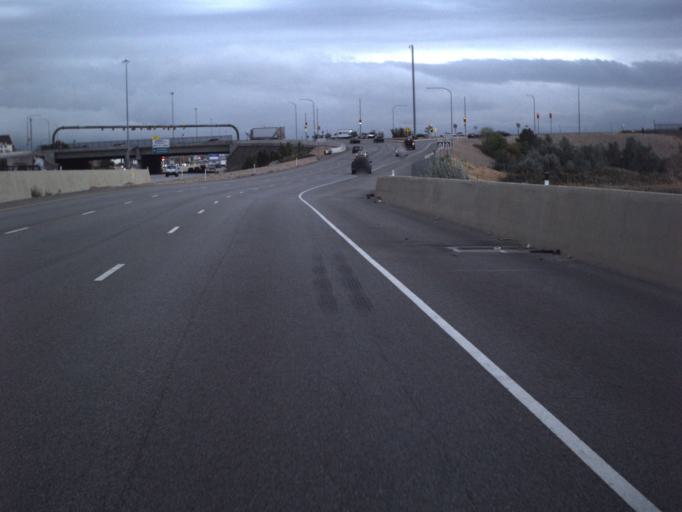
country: US
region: Utah
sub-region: Utah County
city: Orem
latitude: 40.2784
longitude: -111.7221
